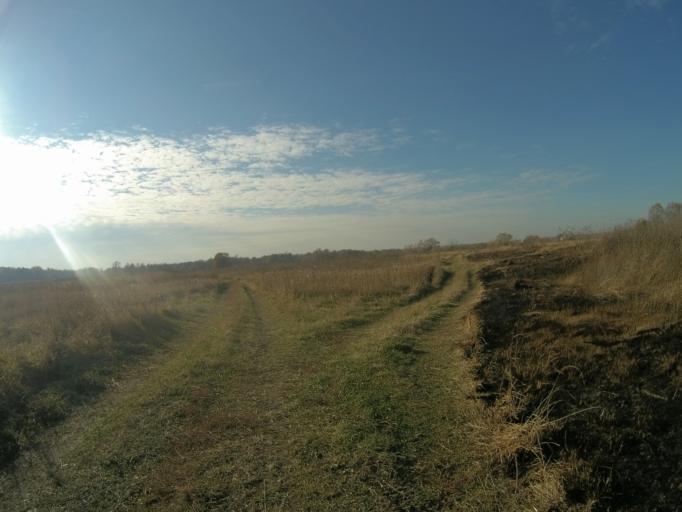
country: RU
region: Vladimir
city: Bogolyubovo
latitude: 56.1841
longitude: 40.5661
